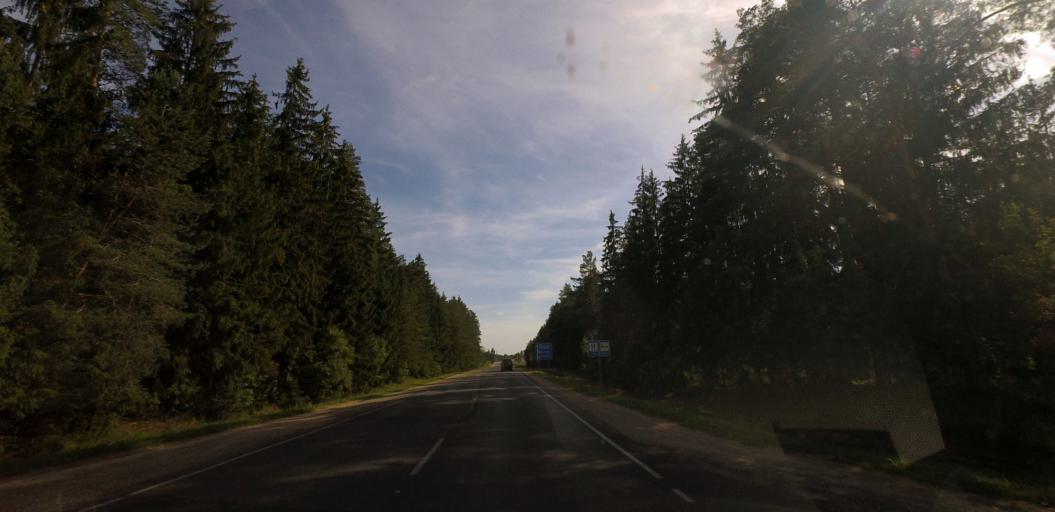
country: BY
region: Grodnenskaya
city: Iwye
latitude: 53.8897
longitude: 25.7445
